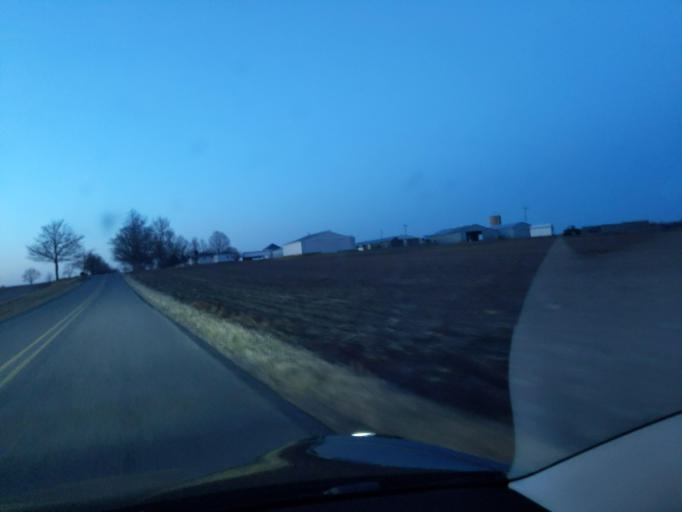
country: US
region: Michigan
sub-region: Ingham County
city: Stockbridge
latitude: 42.5228
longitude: -84.2202
